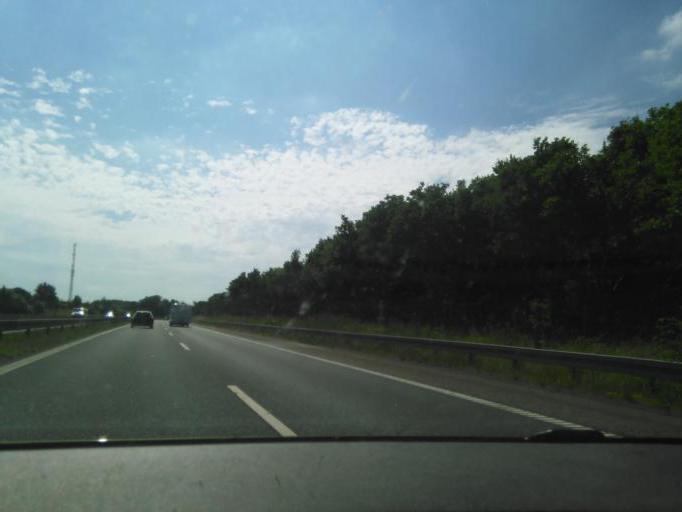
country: DK
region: Zealand
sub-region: Soro Kommune
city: Soro
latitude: 55.4456
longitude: 11.5186
